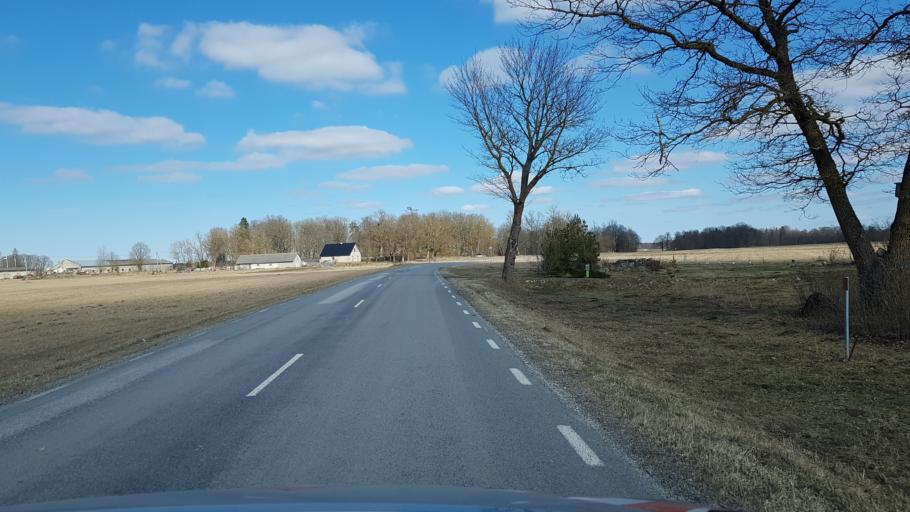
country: EE
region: Laeaene-Virumaa
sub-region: Tapa vald
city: Tapa
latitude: 59.2693
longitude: 25.8560
